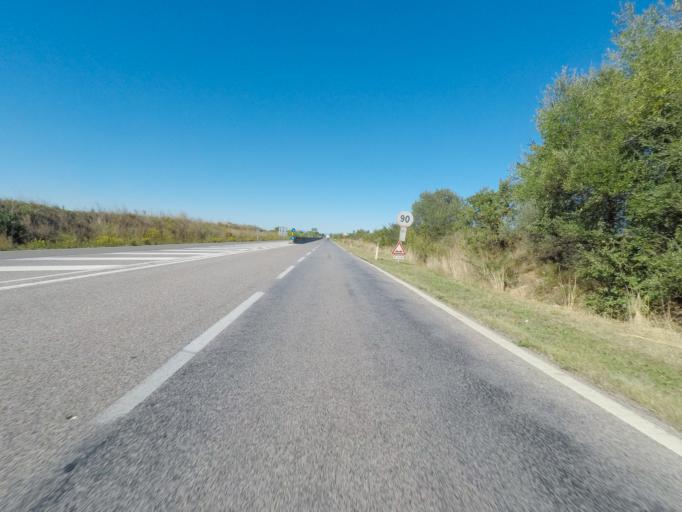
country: IT
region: Tuscany
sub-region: Provincia di Grosseto
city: Grosseto
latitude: 42.6793
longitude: 11.1405
